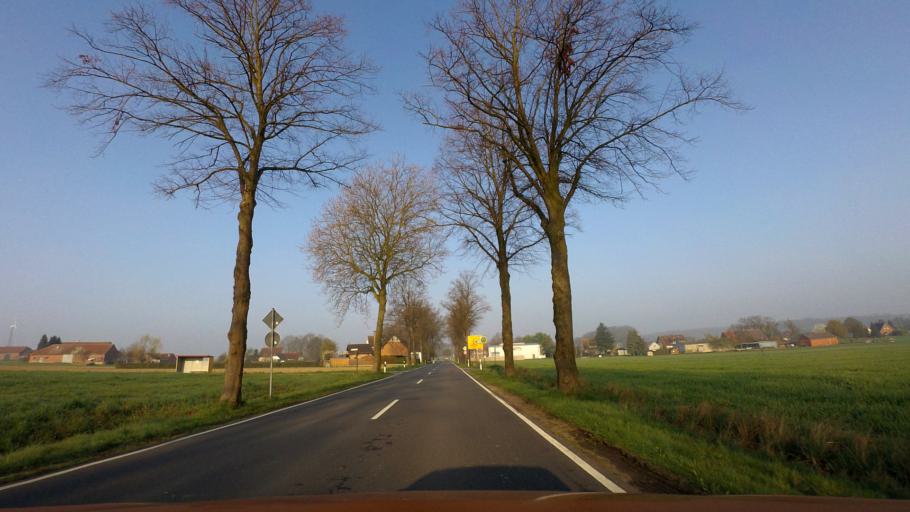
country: DE
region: North Rhine-Westphalia
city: Spenge
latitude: 52.1719
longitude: 8.4731
